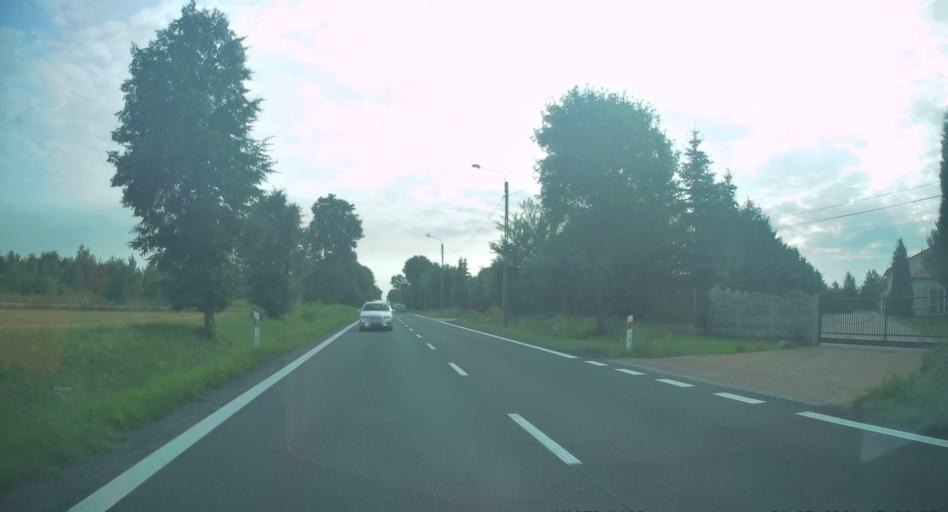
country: PL
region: Silesian Voivodeship
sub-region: Powiat czestochowski
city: Rudniki
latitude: 50.8941
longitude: 19.2746
